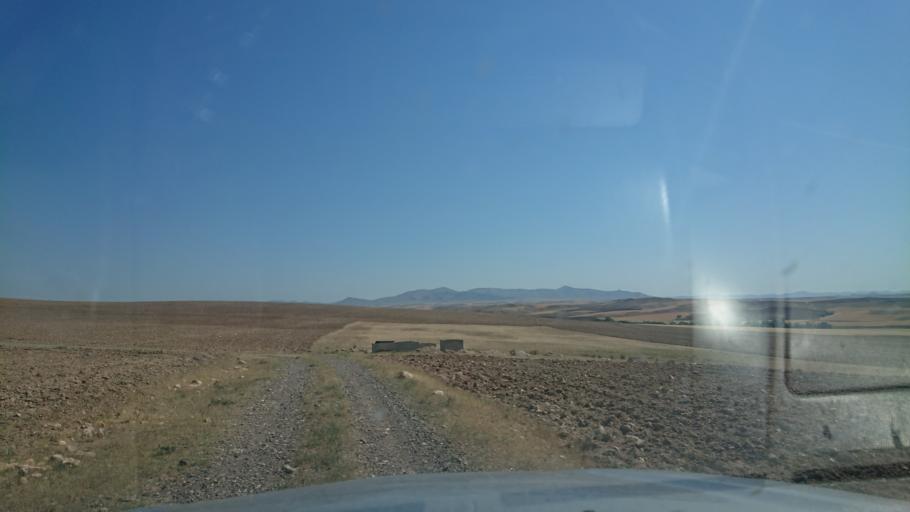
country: TR
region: Aksaray
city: Sariyahsi
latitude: 39.0531
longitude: 33.8892
